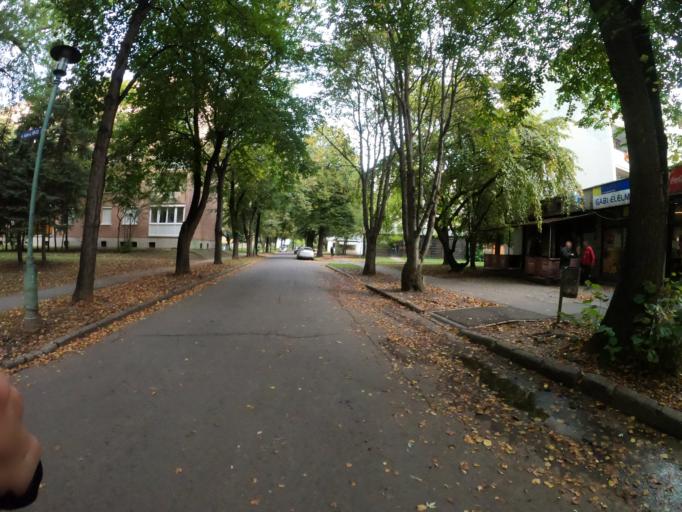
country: HU
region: Borsod-Abauj-Zemplen
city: Miskolc
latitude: 48.0960
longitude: 20.7090
